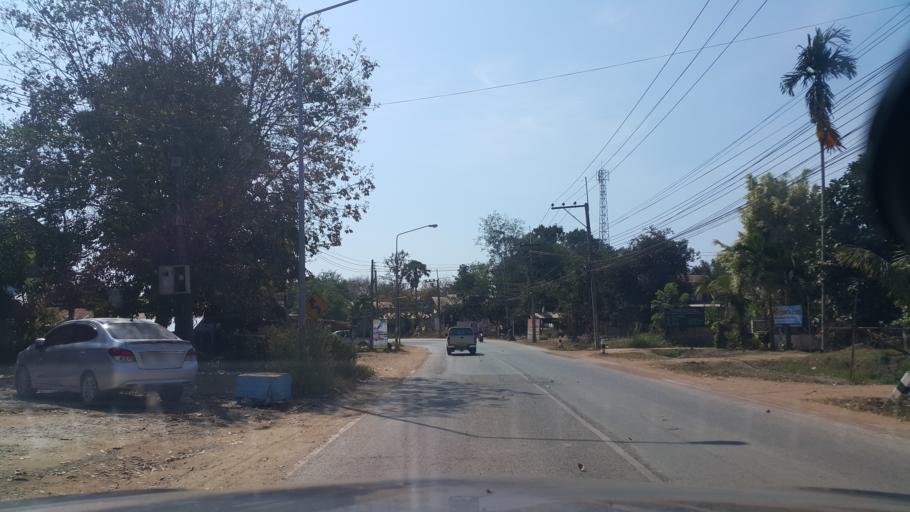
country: TH
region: Changwat Udon Thani
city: Nam Som
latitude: 17.8108
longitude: 102.0977
